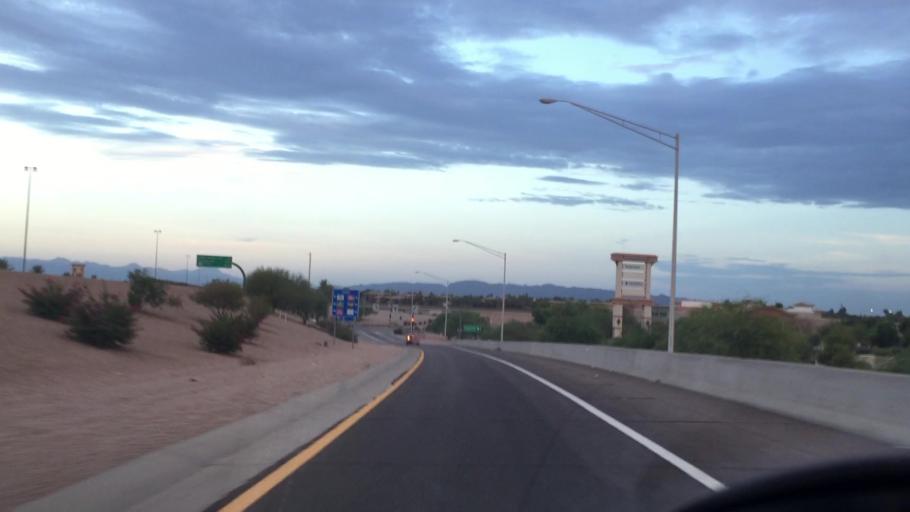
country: US
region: Arizona
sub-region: Maricopa County
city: Chandler
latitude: 33.2876
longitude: -111.8384
